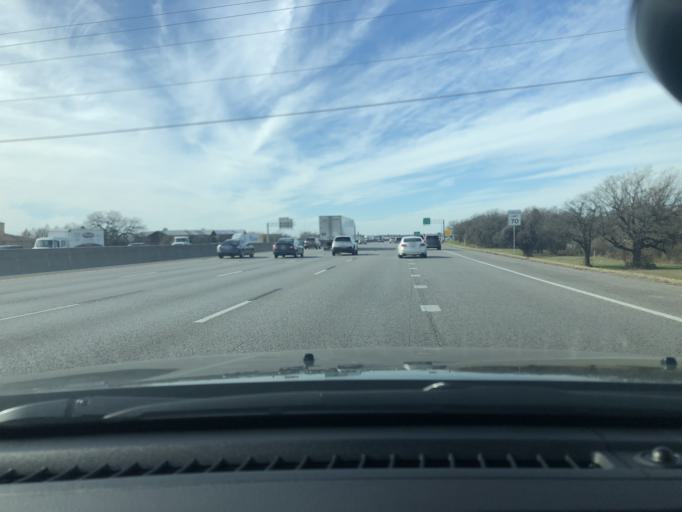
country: US
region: Texas
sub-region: Tarrant County
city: Dalworthington Gardens
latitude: 32.6747
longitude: -97.1435
